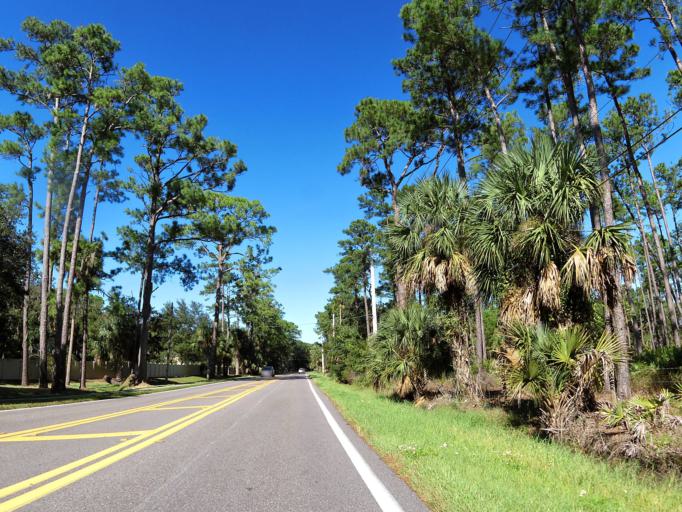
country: US
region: Florida
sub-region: Saint Johns County
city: Palm Valley
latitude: 30.1381
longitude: -81.3802
